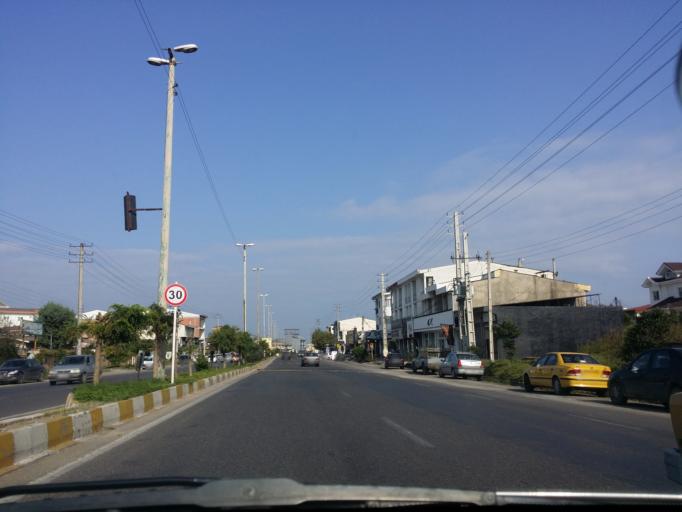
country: IR
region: Mazandaran
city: Chalus
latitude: 36.6759
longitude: 51.4046
